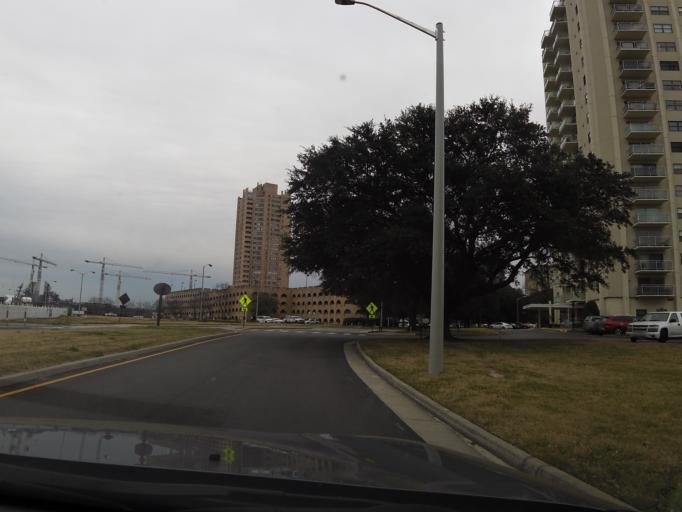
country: US
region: Virginia
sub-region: City of Portsmouth
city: Portsmouth
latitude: 36.8401
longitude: -76.2993
